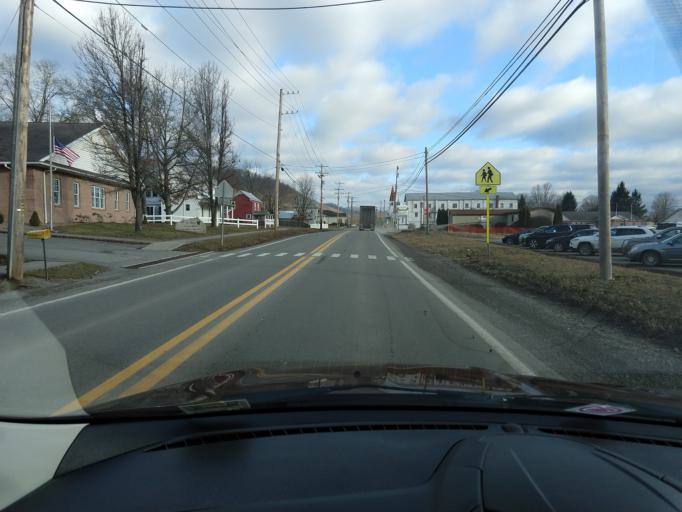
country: US
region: West Virginia
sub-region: Randolph County
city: Elkins
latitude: 38.7291
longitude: -79.9714
